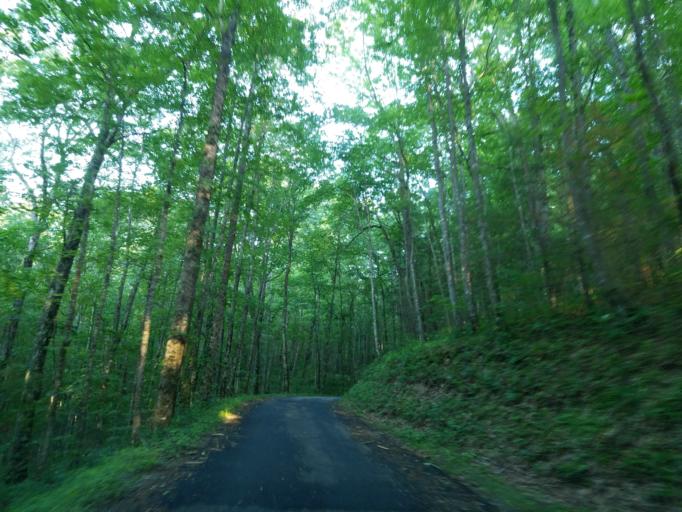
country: US
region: Georgia
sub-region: Union County
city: Blairsville
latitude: 34.7093
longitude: -84.0178
